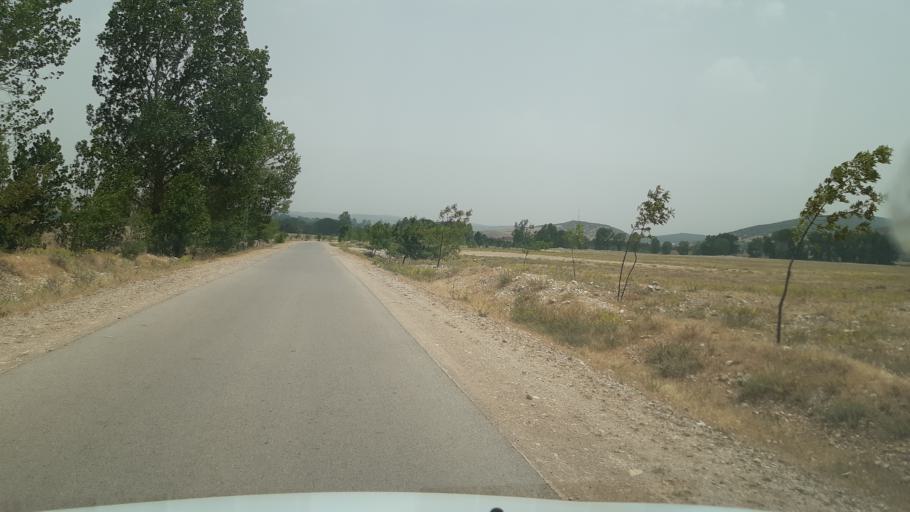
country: MA
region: Meknes-Tafilalet
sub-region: Ifrane
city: Ifrane
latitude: 33.6480
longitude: -5.0255
